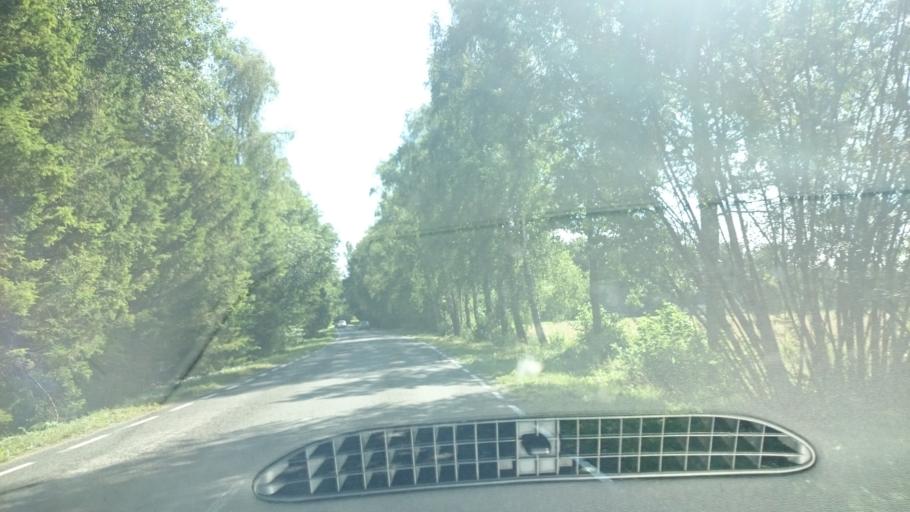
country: EE
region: Saare
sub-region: Kuressaare linn
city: Kuressaare
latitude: 58.5780
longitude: 22.6871
